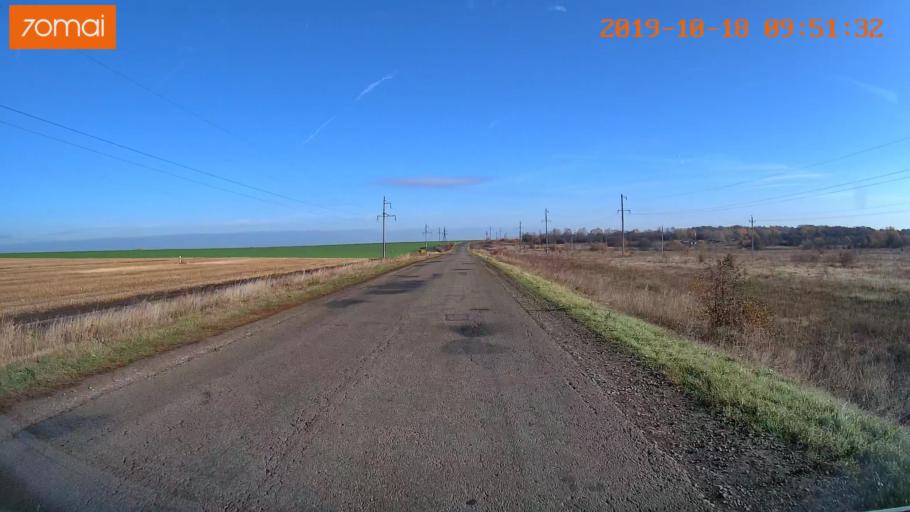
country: RU
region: Tula
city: Kazachka
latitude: 53.3419
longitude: 38.2942
